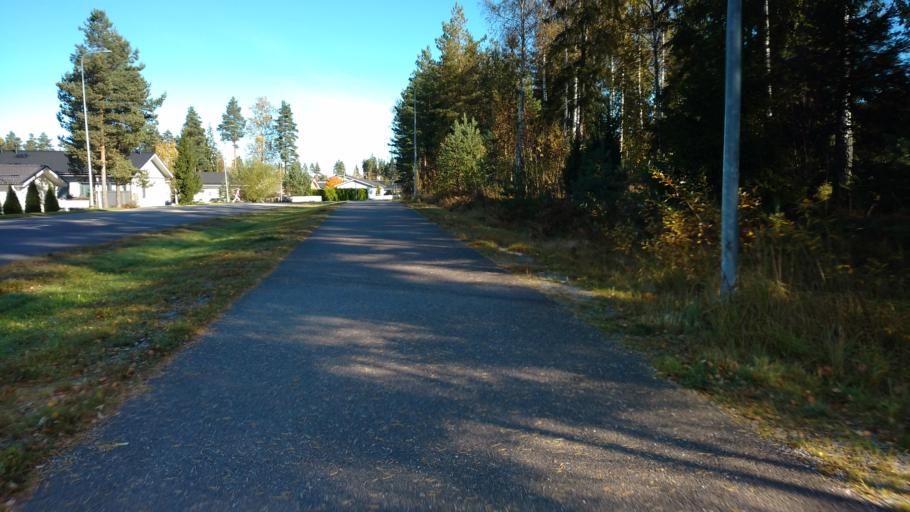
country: FI
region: Varsinais-Suomi
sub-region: Salo
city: Salo
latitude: 60.3996
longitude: 23.1844
